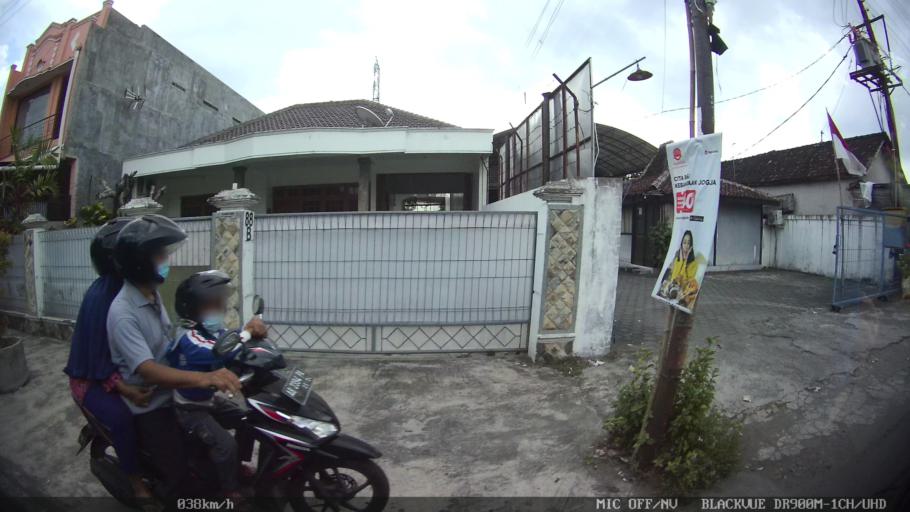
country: ID
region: Daerah Istimewa Yogyakarta
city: Yogyakarta
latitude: -7.7828
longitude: 110.3423
